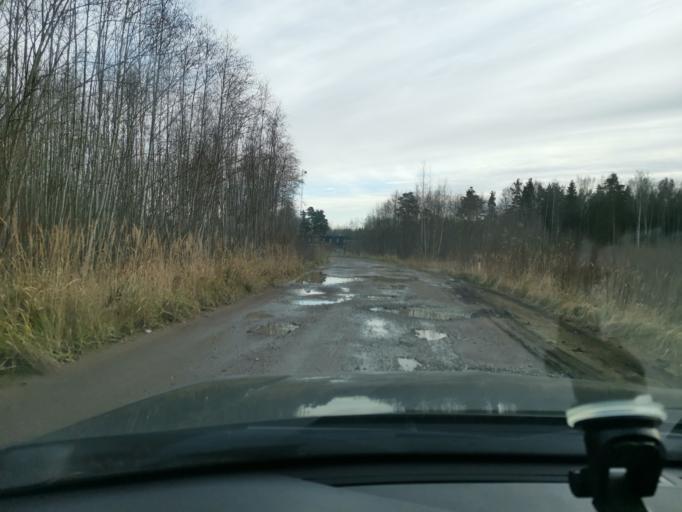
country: EE
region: Ida-Virumaa
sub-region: Sillamaee linn
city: Sillamae
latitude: 59.2587
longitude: 27.9130
